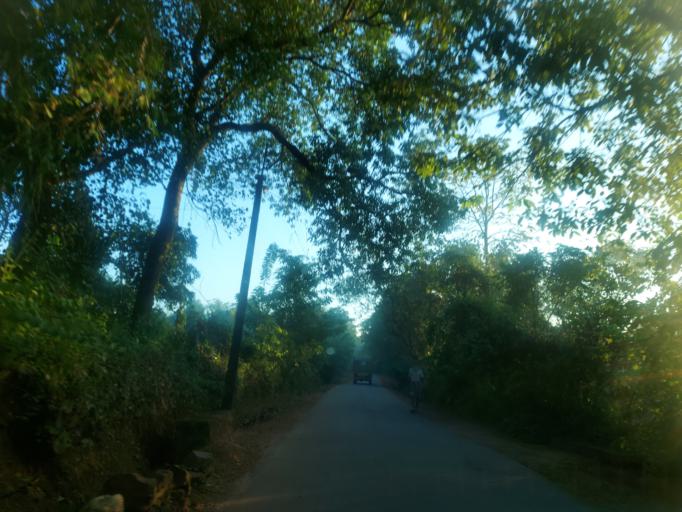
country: IN
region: Maharashtra
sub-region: Sindhudurg
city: Kudal
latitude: 16.0514
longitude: 73.7113
